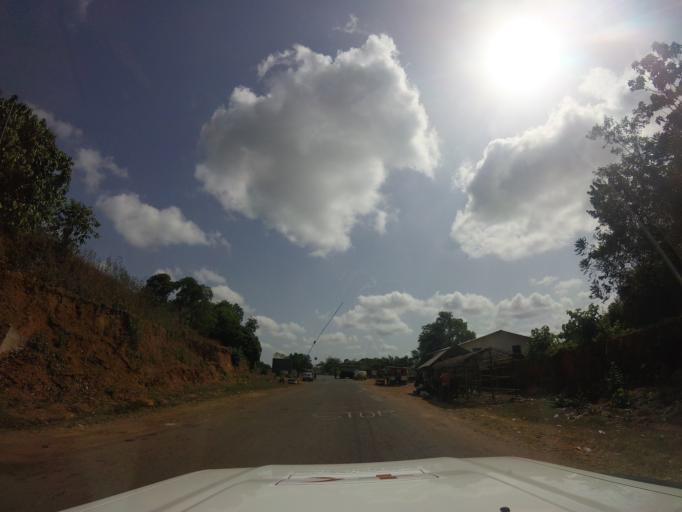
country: LR
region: Grand Cape Mount
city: Robertsport
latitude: 6.8127
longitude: -11.1388
